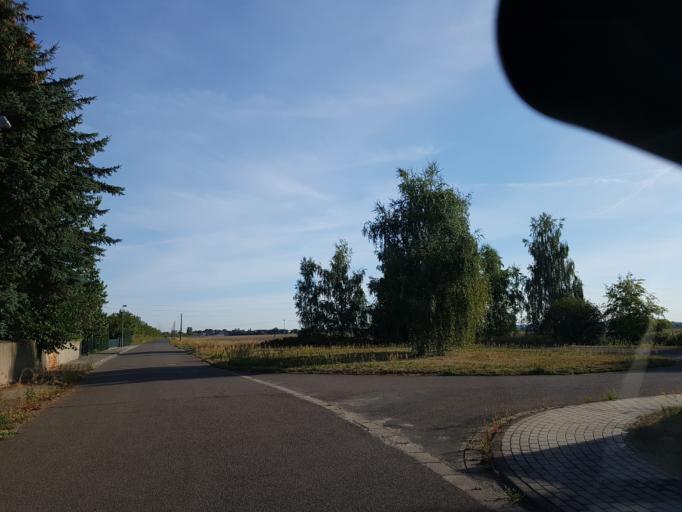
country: DE
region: Saxony
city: Nauwalde
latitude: 51.4480
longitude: 13.4194
